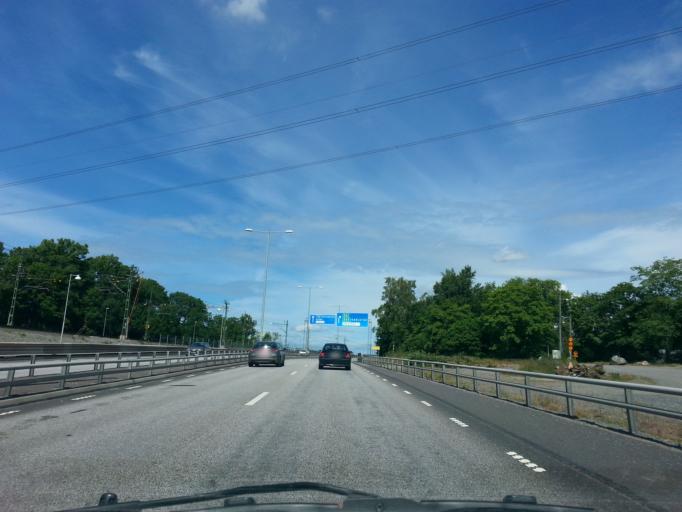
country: SE
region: Vaestra Goetaland
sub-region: Goteborg
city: Hammarkullen
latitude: 57.7595
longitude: 12.0049
